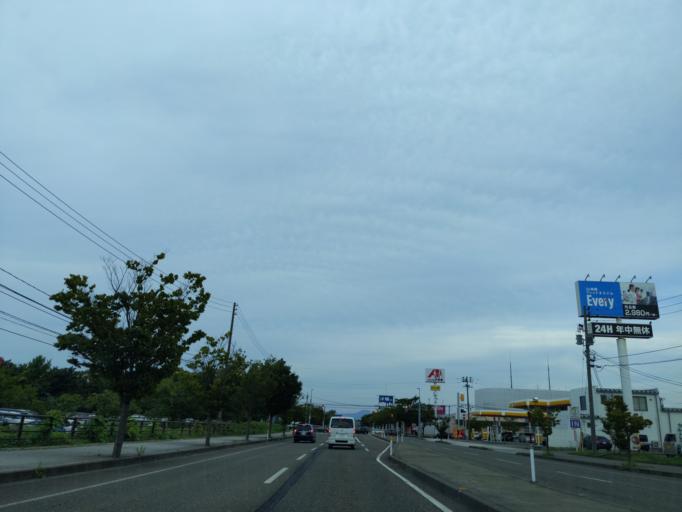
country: JP
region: Niigata
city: Joetsu
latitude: 37.1521
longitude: 138.2506
